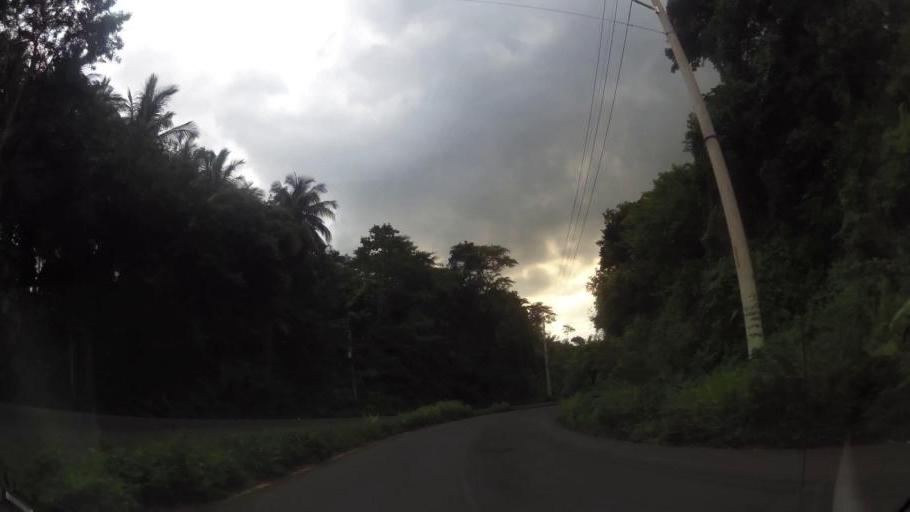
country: GT
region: Escuintla
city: Santa Lucia Cotzumalguapa
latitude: 14.3628
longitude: -91.0976
